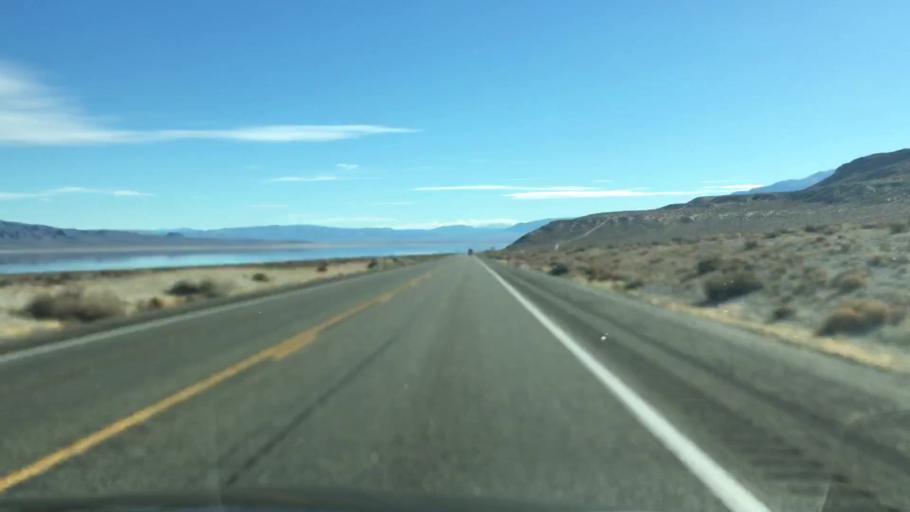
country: US
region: Nevada
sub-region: Mineral County
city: Hawthorne
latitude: 38.7920
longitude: -118.7558
